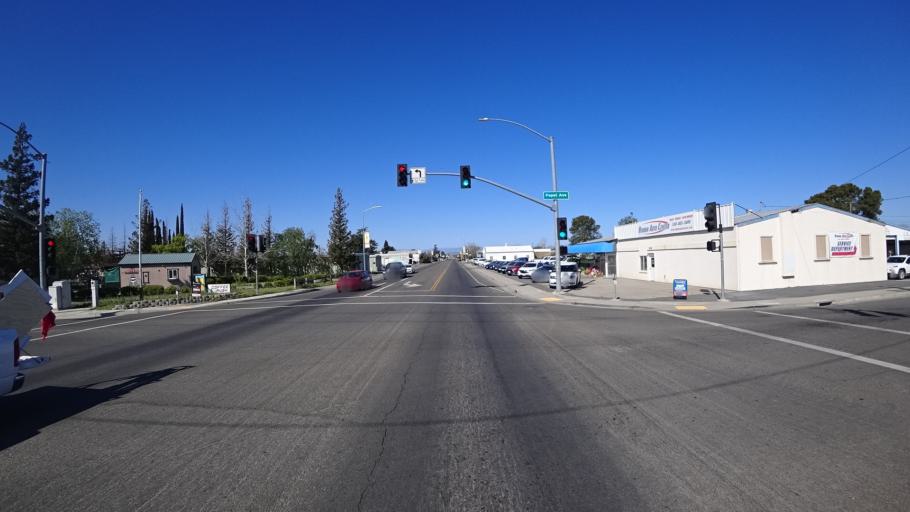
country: US
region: California
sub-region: Glenn County
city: Orland
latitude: 39.7473
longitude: -122.1781
